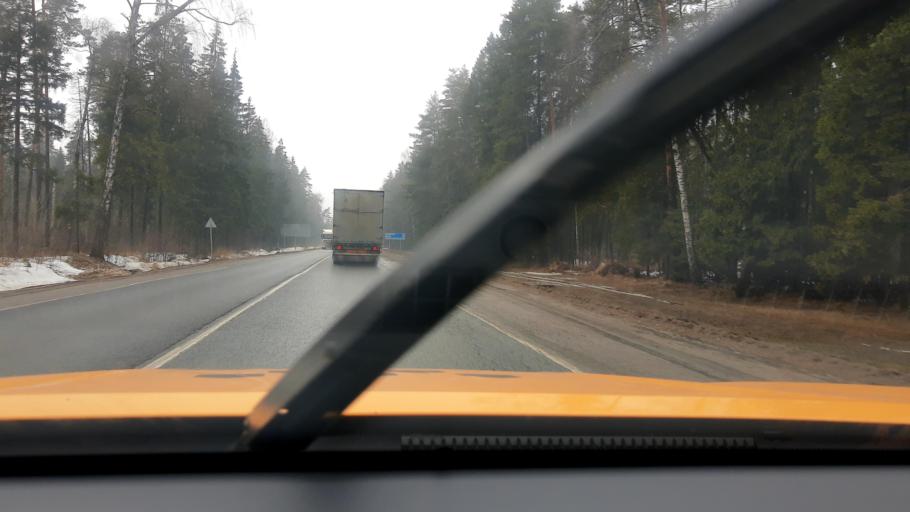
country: RU
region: Moskovskaya
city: Chernogolovka
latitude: 55.9860
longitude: 38.3367
